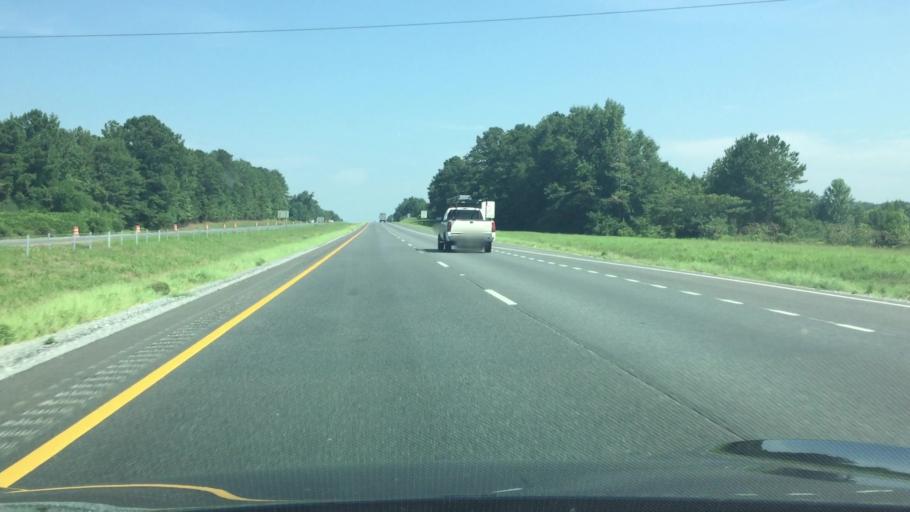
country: US
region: Alabama
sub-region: Chilton County
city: Clanton
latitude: 32.8067
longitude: -86.5819
